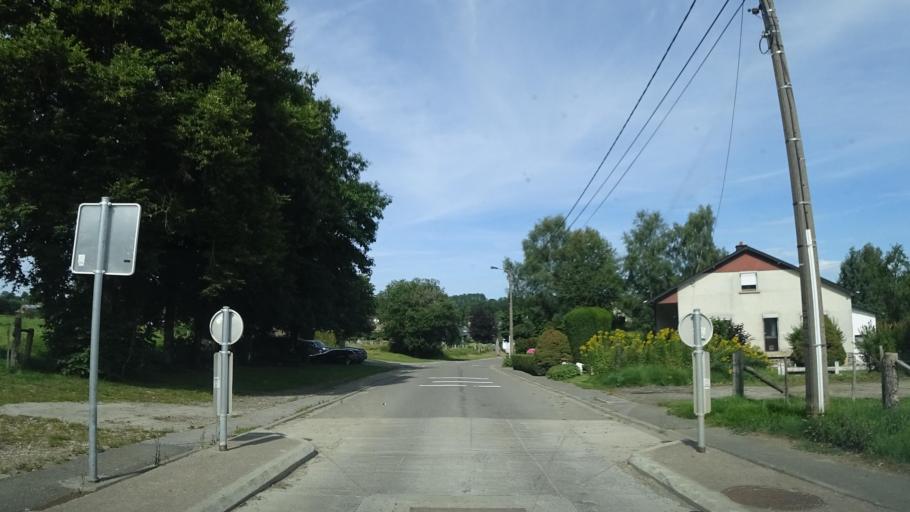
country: BE
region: Wallonia
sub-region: Province du Luxembourg
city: Bertrix
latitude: 49.8185
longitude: 5.3276
